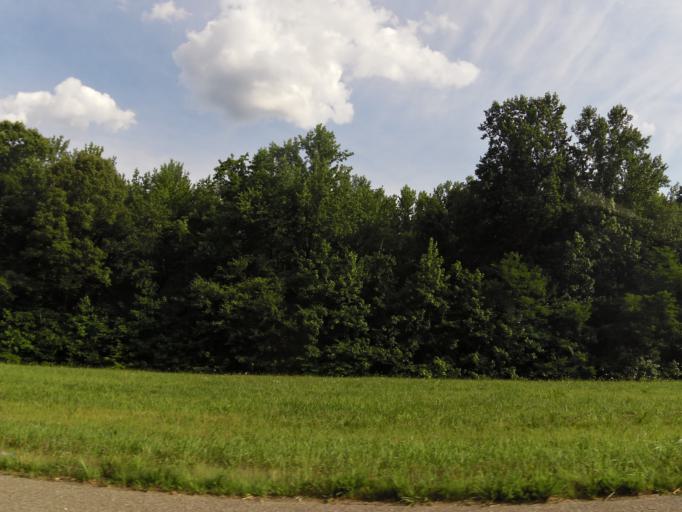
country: US
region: Tennessee
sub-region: Benton County
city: Camden
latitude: 36.0266
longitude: -88.0787
